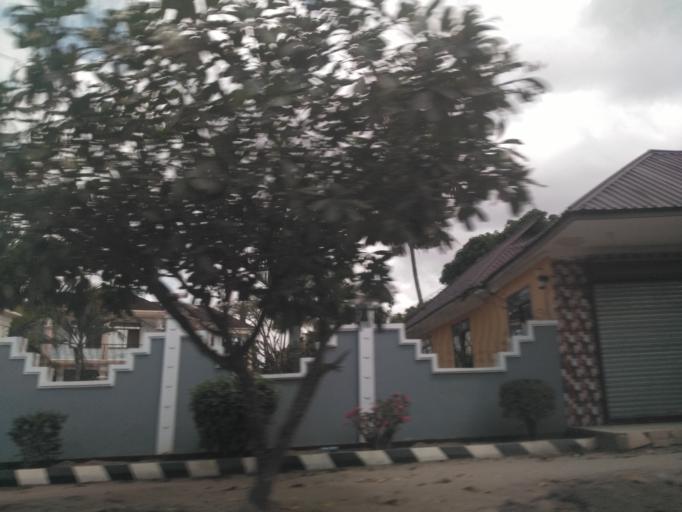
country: TZ
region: Dar es Salaam
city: Dar es Salaam
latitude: -6.8899
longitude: 39.2872
